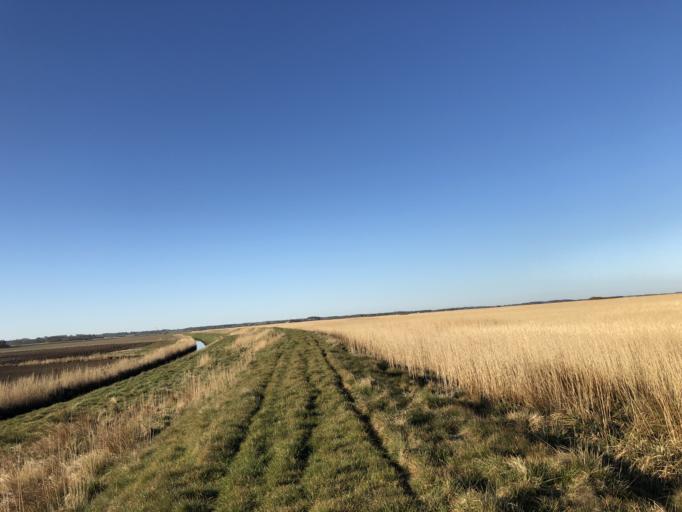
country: DK
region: Central Jutland
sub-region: Holstebro Kommune
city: Ulfborg
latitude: 56.3085
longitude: 8.2932
